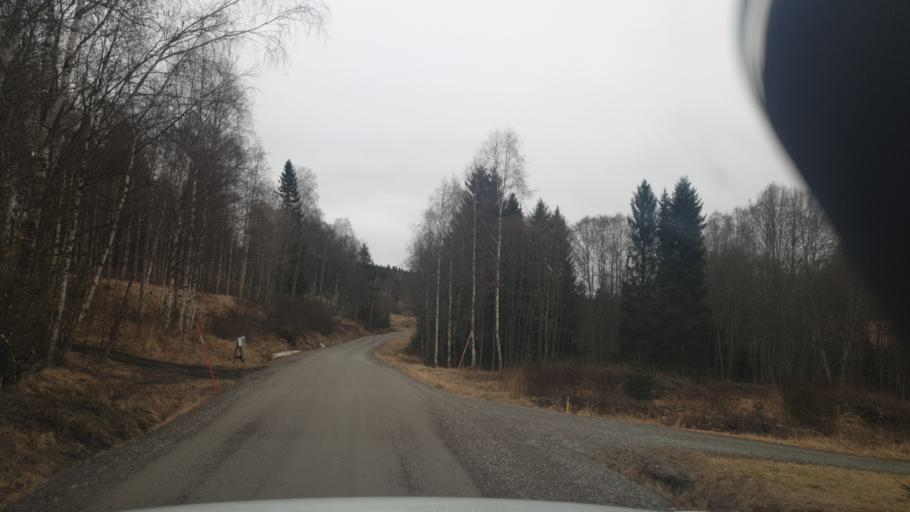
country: NO
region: Ostfold
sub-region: Romskog
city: Romskog
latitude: 59.6825
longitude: 11.9315
